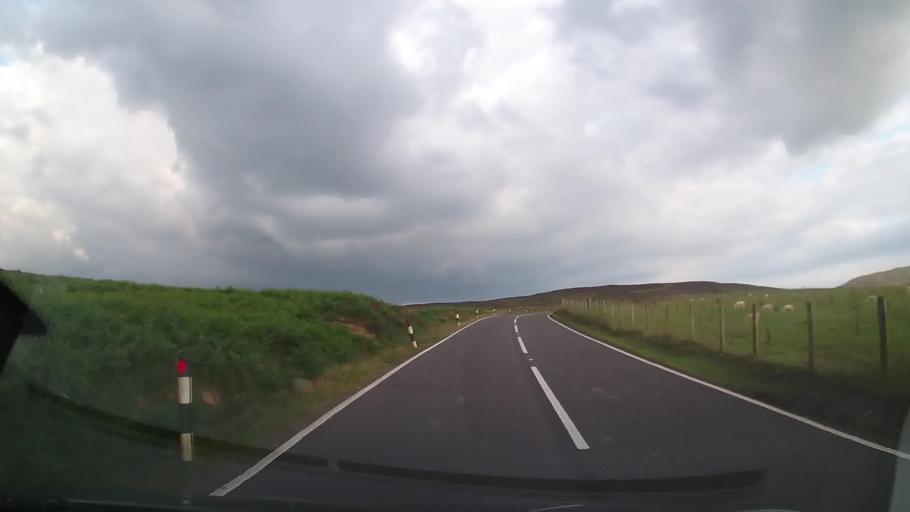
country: GB
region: Wales
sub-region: Denbighshire
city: Llandrillo
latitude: 52.8955
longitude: -3.4887
